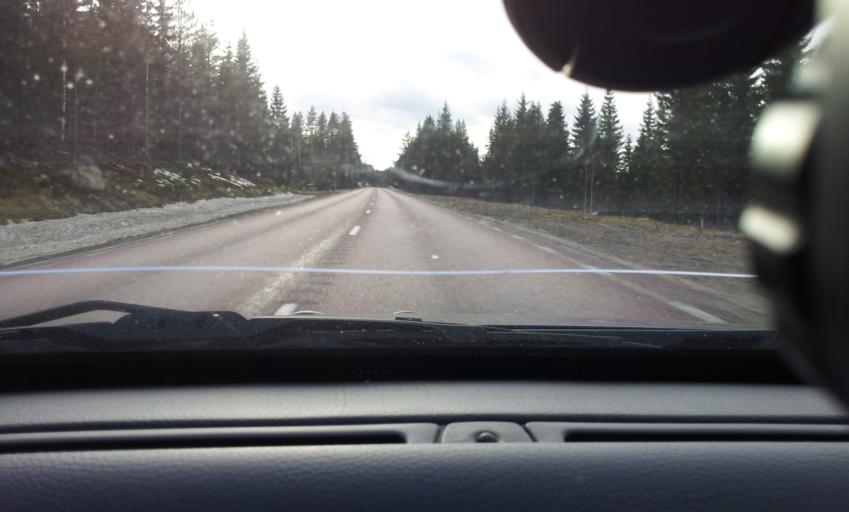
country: SE
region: Gaevleborg
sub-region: Ljusdals Kommun
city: Farila
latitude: 61.8874
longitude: 15.6908
